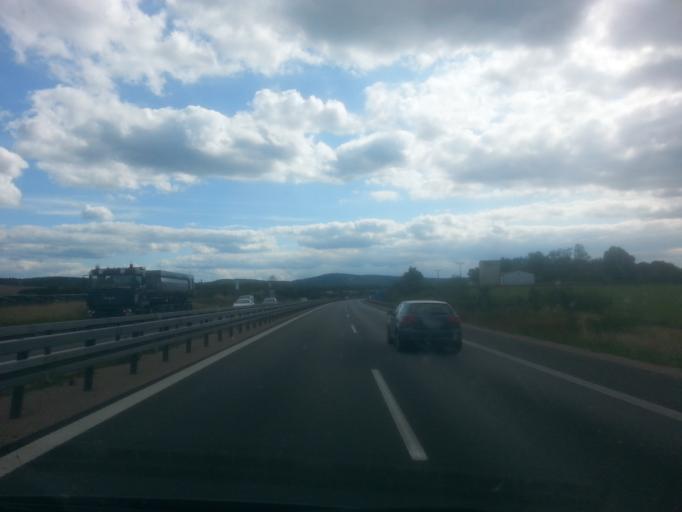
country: DE
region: Bavaria
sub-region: Upper Palatinate
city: Nabburg
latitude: 49.4683
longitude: 12.1944
